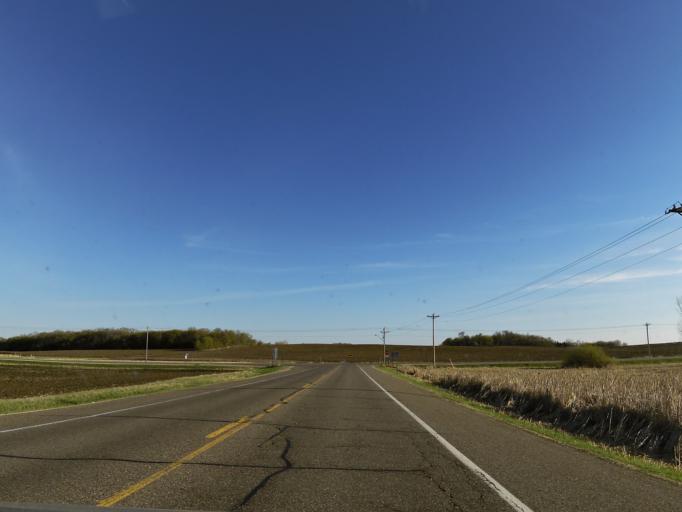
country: US
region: Minnesota
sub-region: Rice County
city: Northfield
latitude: 44.5449
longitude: -93.2076
